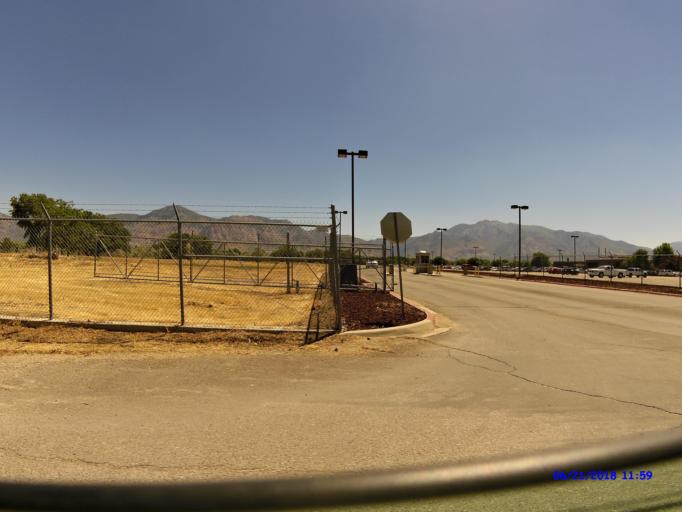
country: US
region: Utah
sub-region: Weber County
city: Marriott-Slaterville
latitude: 41.2492
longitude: -112.0095
